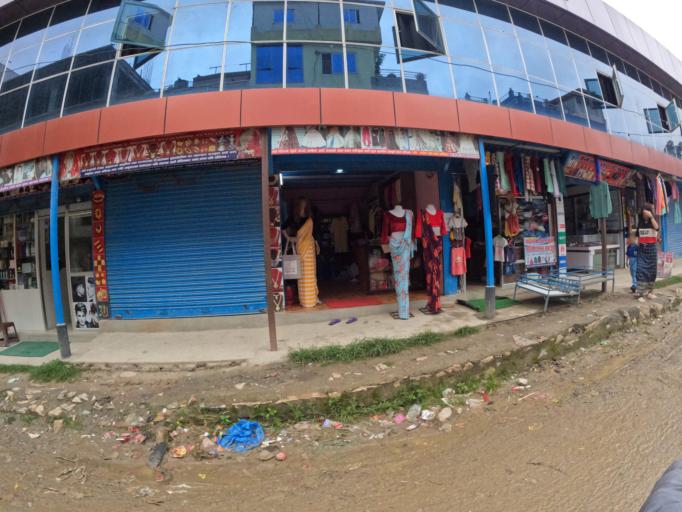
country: NP
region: Central Region
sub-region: Bagmati Zone
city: Kathmandu
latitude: 27.7616
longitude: 85.3177
